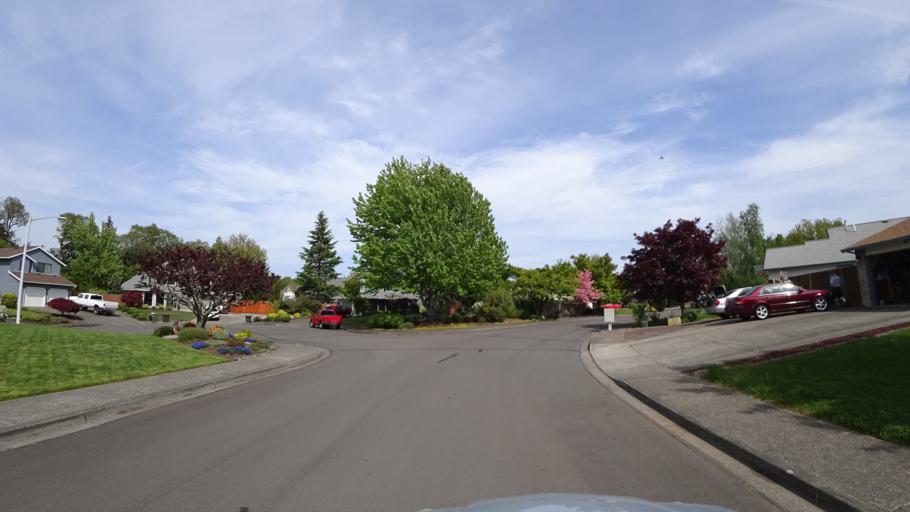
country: US
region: Oregon
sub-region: Washington County
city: Rockcreek
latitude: 45.5374
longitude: -122.9293
